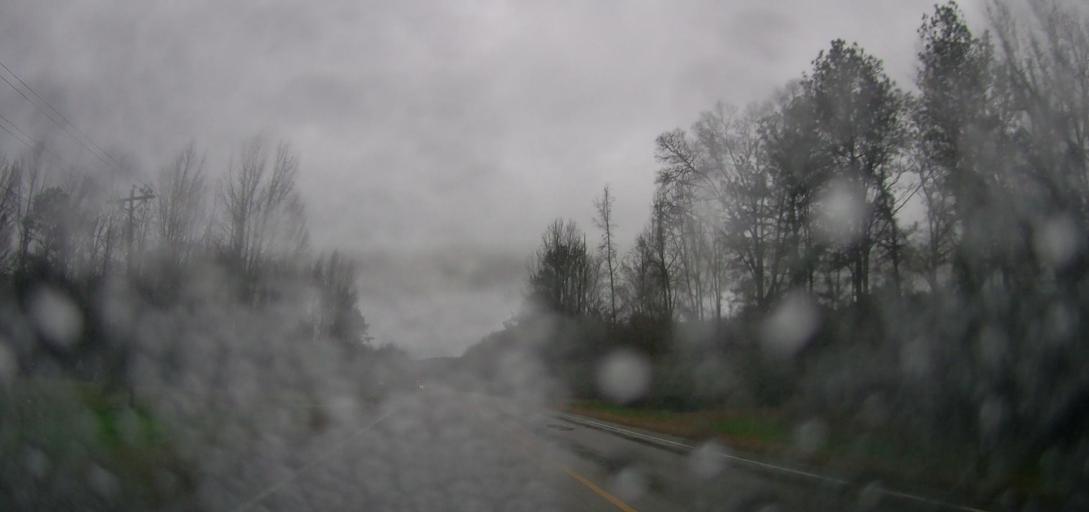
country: US
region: Alabama
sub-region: Autauga County
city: Prattville
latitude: 32.5062
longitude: -86.5861
